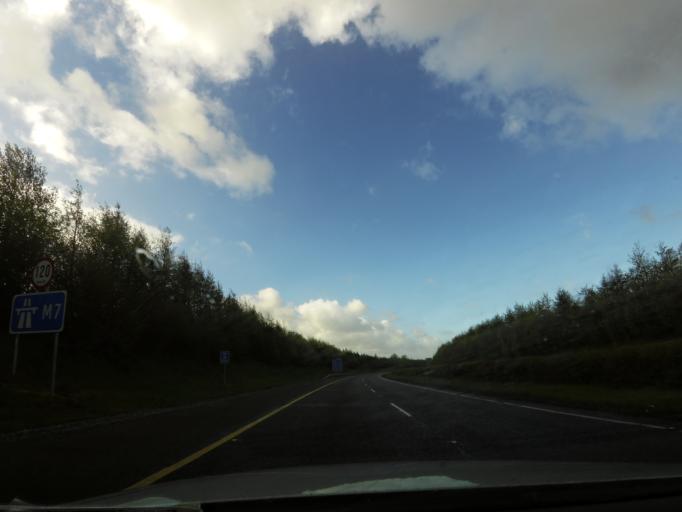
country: IE
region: Munster
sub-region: County Limerick
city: Annacotty
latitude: 52.6657
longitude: -8.5165
